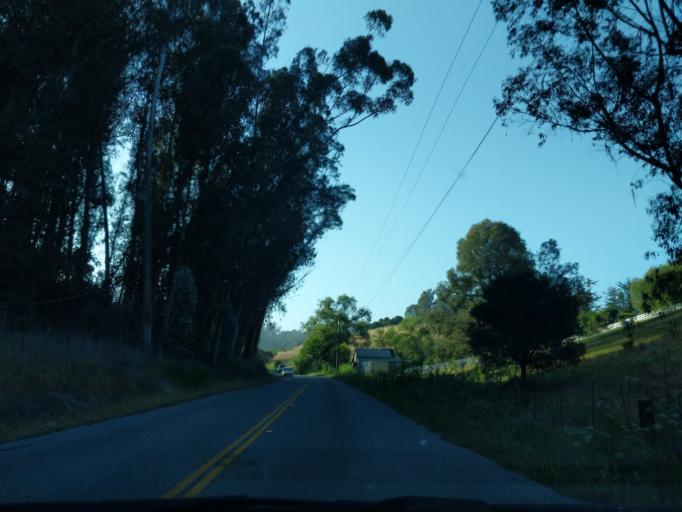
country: US
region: California
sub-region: Monterey County
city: Las Lomas
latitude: 36.8636
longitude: -121.6882
